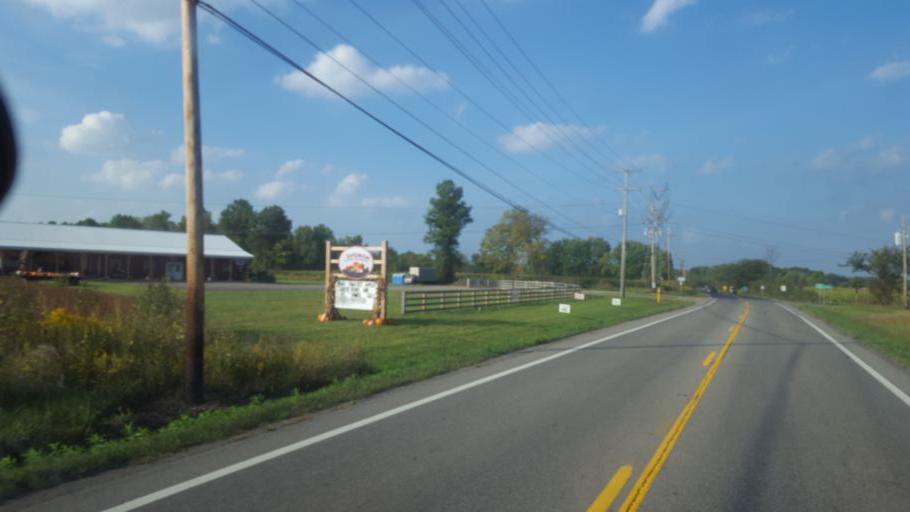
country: US
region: Ohio
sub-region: Franklin County
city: New Albany
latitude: 40.1212
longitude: -82.7610
